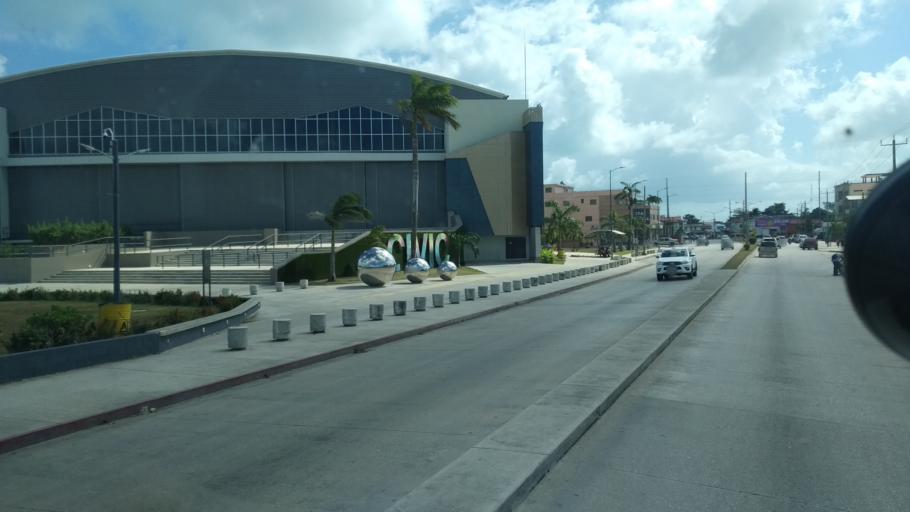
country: BZ
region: Belize
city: Belize City
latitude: 17.5022
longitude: -88.1978
